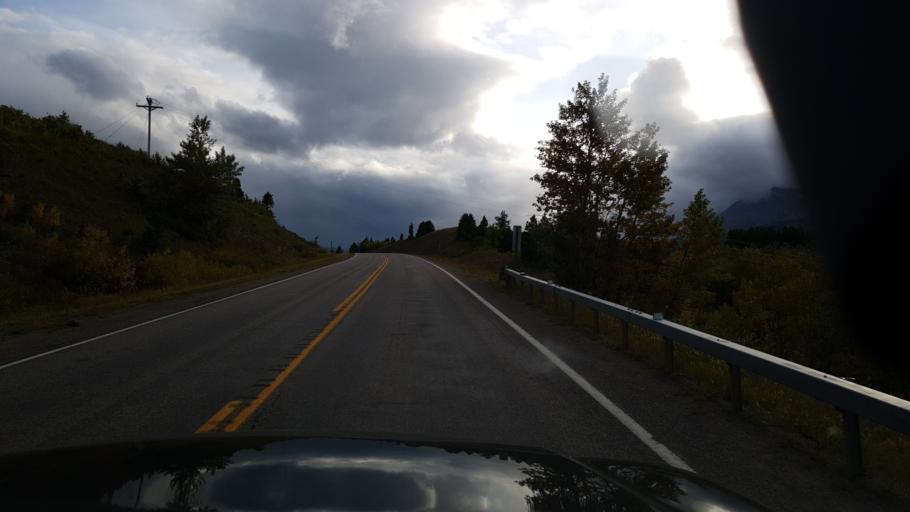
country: US
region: Montana
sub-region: Glacier County
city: South Browning
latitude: 48.3831
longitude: -113.2719
